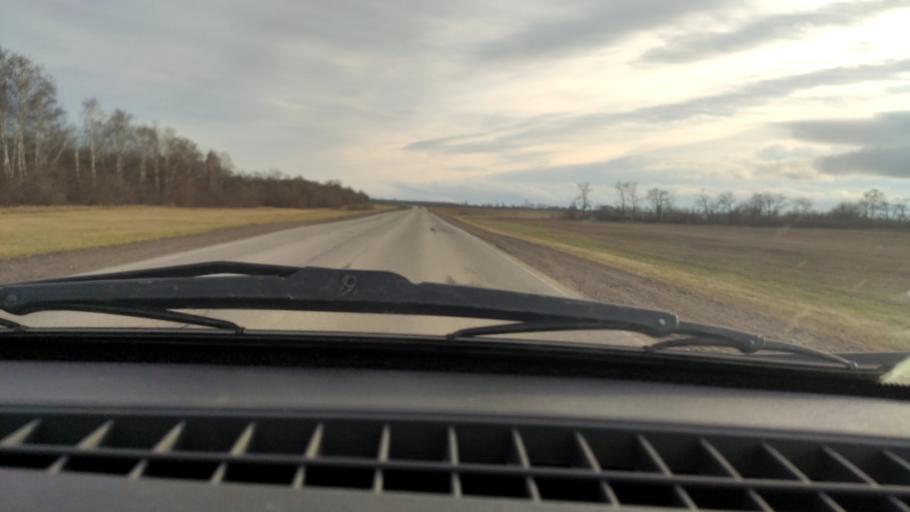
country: RU
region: Bashkortostan
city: Davlekanovo
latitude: 54.2824
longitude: 55.1108
